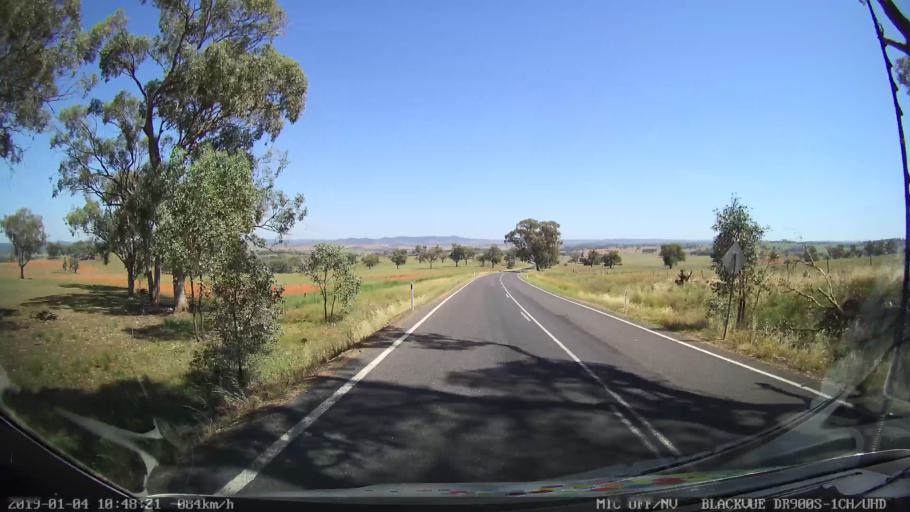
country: AU
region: New South Wales
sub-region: Cabonne
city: Molong
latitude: -33.2611
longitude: 148.7135
